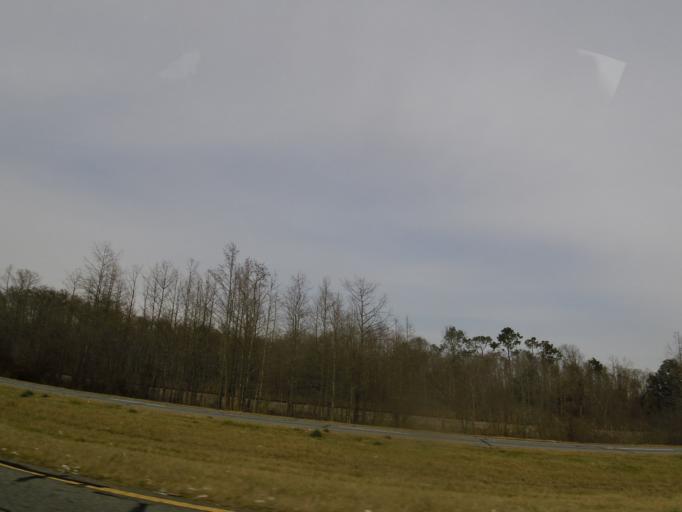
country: US
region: Georgia
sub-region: Seminole County
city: Donalsonville
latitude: 31.0267
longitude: -84.8445
